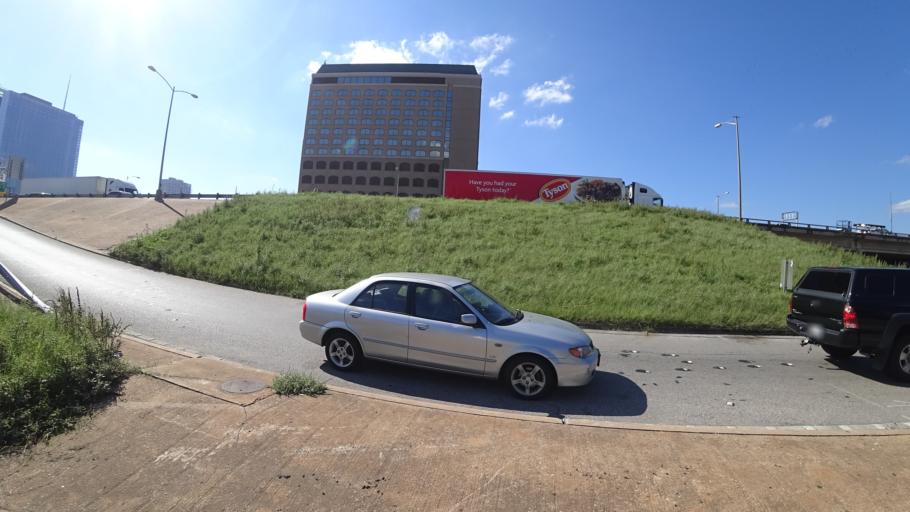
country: US
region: Texas
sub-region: Travis County
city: Austin
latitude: 30.2652
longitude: -97.7343
